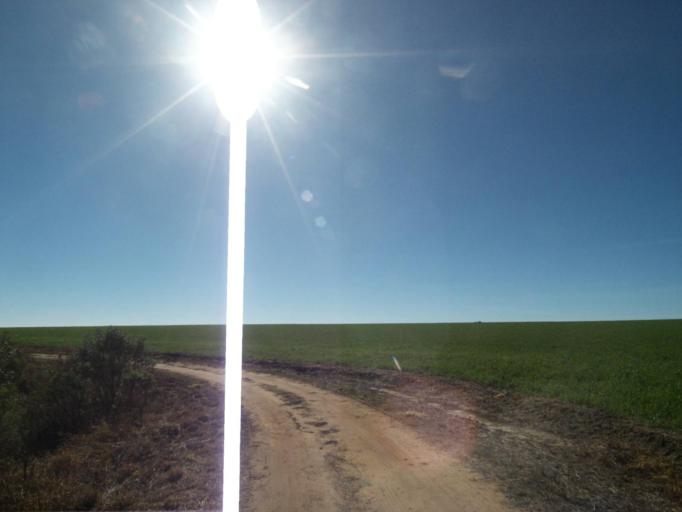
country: BR
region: Parana
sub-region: Tibagi
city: Tibagi
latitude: -24.5924
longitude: -50.2497
